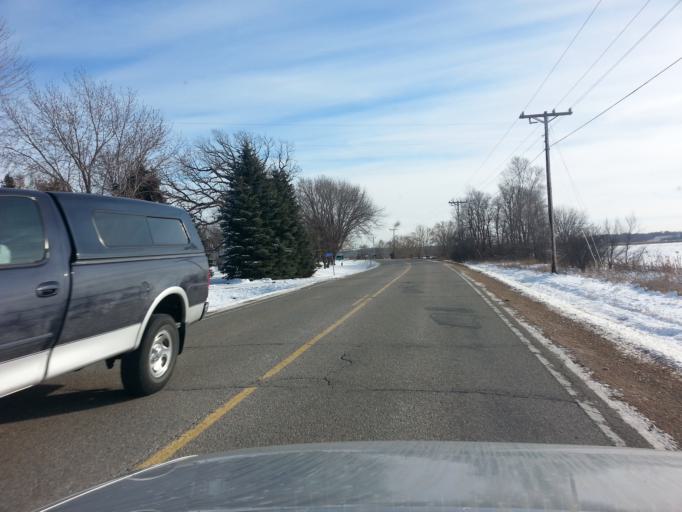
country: US
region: Minnesota
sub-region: Scott County
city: Prior Lake
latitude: 44.7731
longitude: -93.4562
